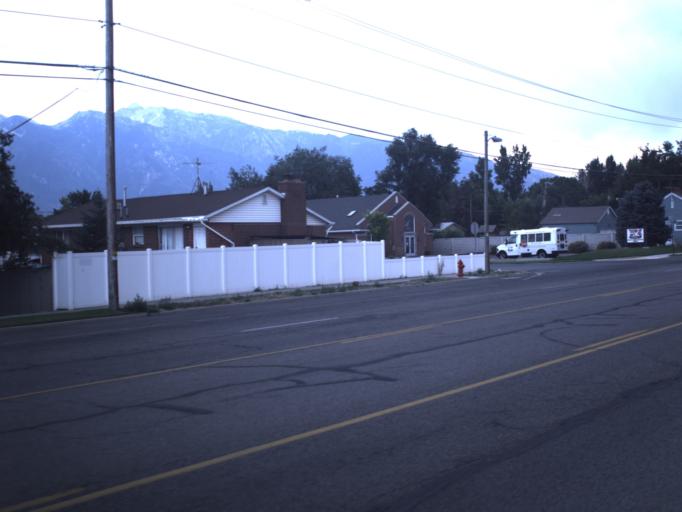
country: US
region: Utah
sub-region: Salt Lake County
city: Sandy City
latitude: 40.6015
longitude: -111.8723
